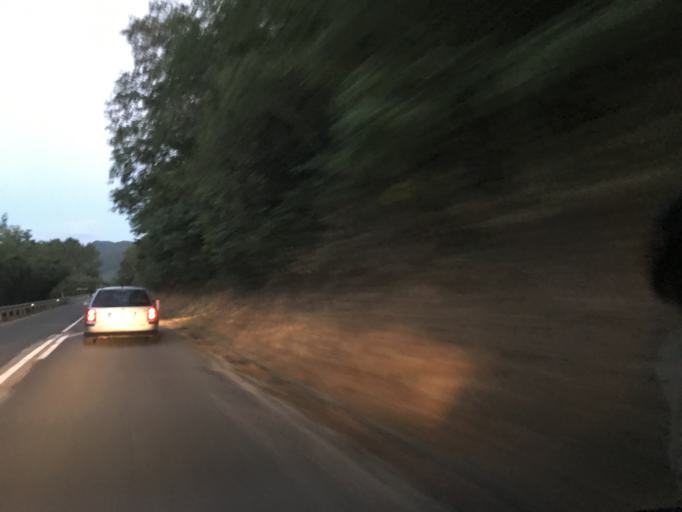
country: RO
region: Caras-Severin
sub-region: Comuna Berzasca
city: Berzasca
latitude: 44.6391
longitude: 21.9265
